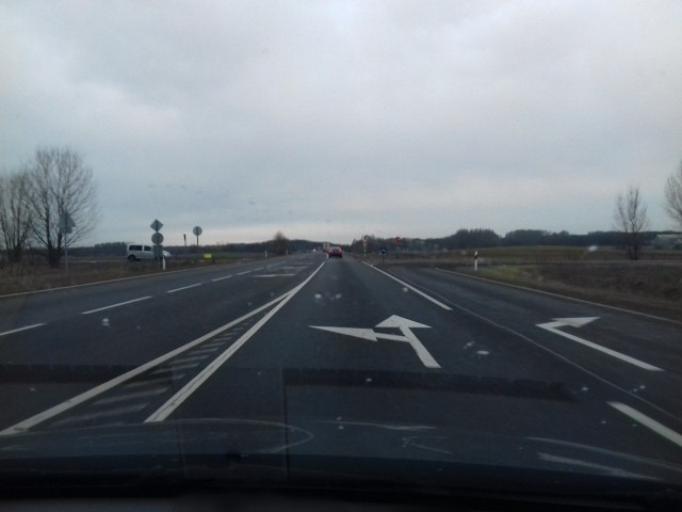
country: HU
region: Szabolcs-Szatmar-Bereg
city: Napkor
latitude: 47.9359
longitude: 21.8185
